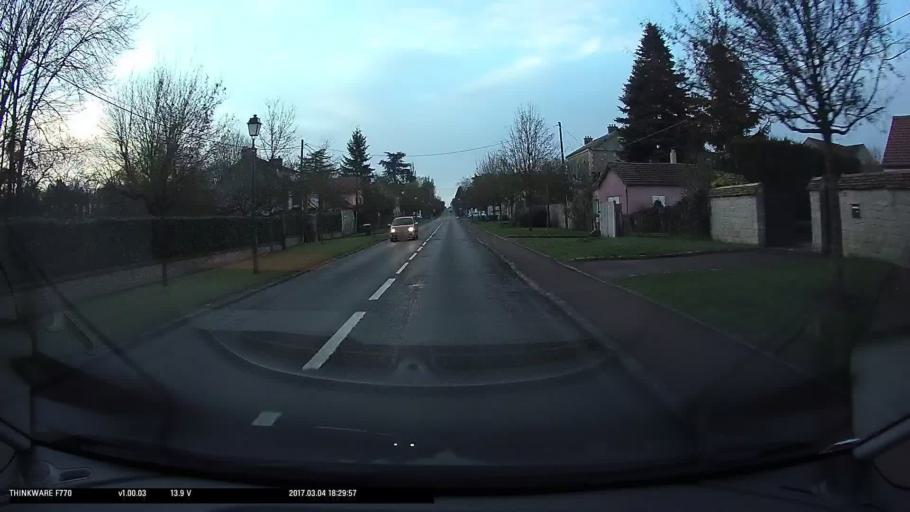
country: FR
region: Ile-de-France
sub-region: Departement du Val-d'Oise
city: Marines
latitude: 49.1383
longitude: 1.9861
